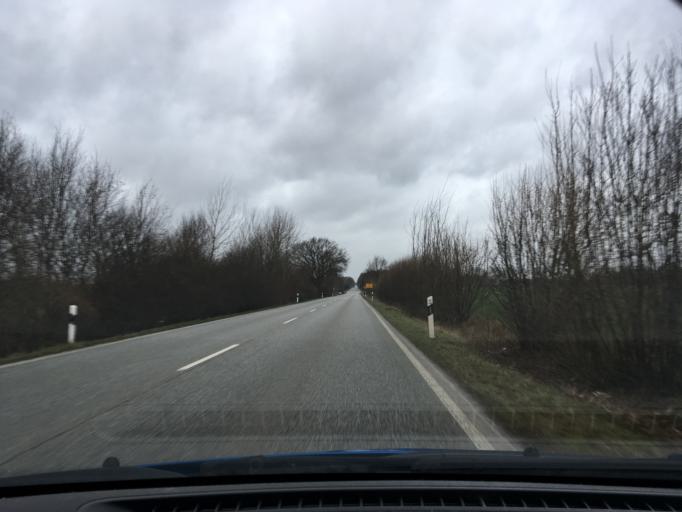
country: DE
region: Schleswig-Holstein
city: Wangelau
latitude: 53.4507
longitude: 10.5545
